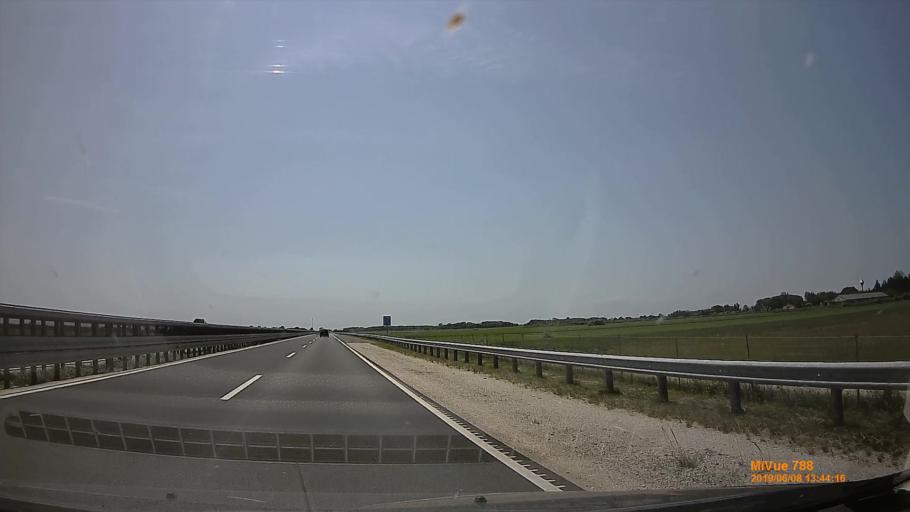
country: HU
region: Gyor-Moson-Sopron
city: Beled
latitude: 47.4430
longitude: 17.0908
